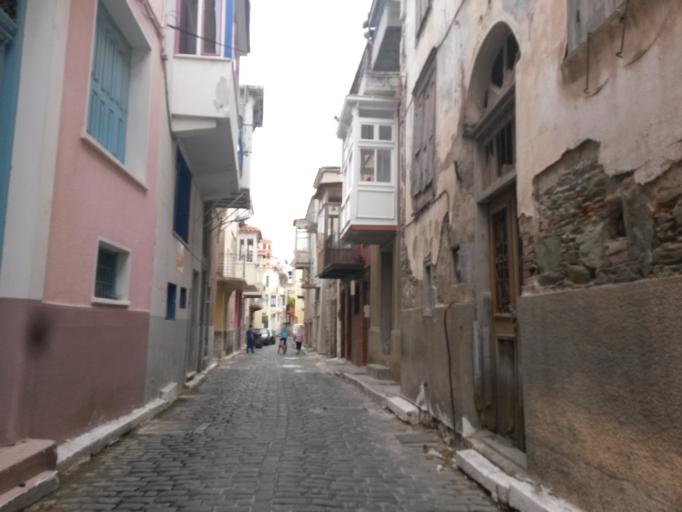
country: GR
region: North Aegean
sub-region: Nomos Lesvou
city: Plomarion
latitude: 38.9773
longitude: 26.3706
